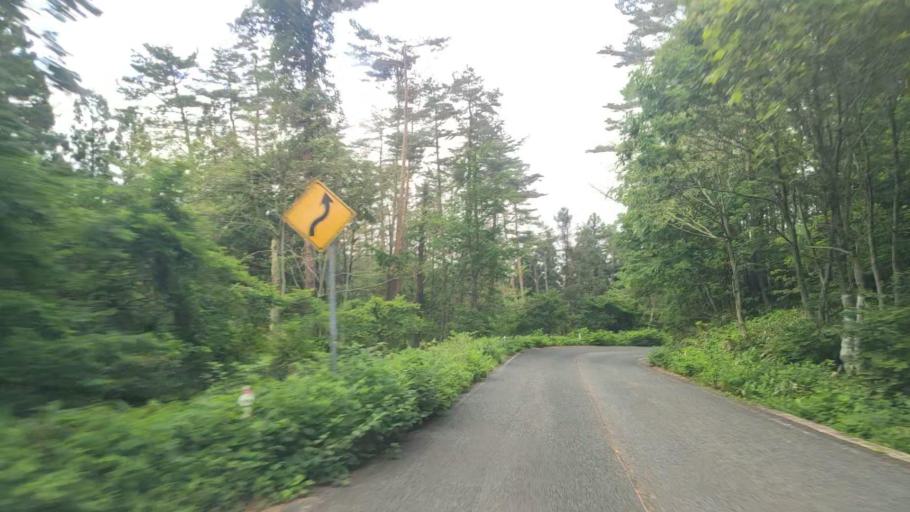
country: JP
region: Tottori
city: Yonago
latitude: 35.3300
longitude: 133.5697
